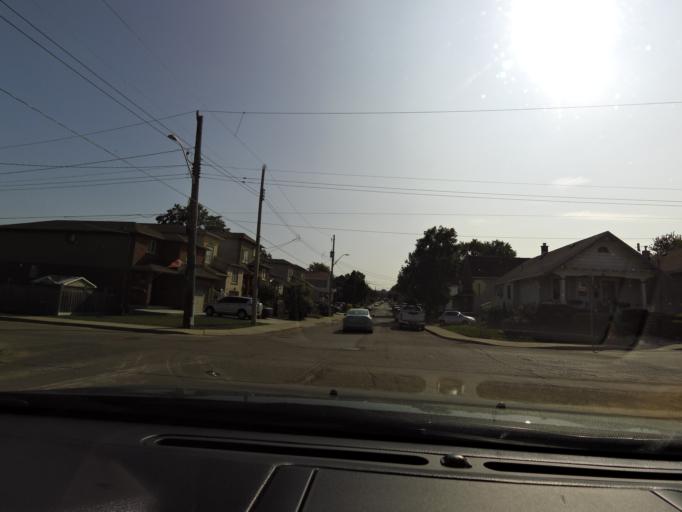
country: CA
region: Ontario
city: Hamilton
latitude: 43.2677
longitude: -79.8586
